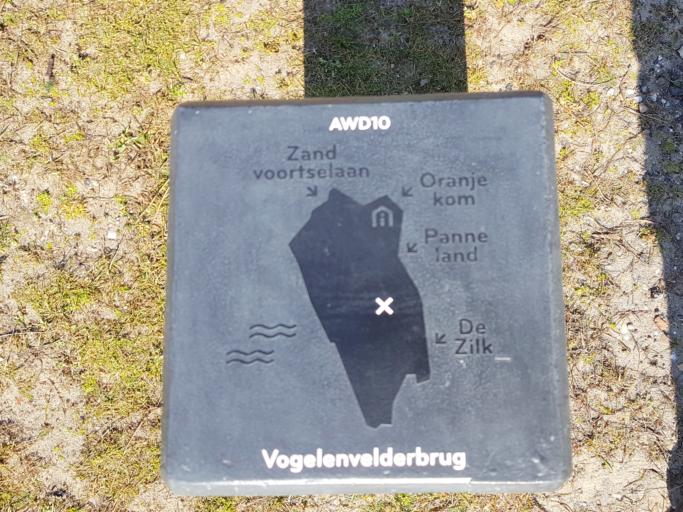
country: NL
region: South Holland
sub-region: Gemeente Hillegom
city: Hillegom
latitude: 52.3131
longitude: 4.5404
